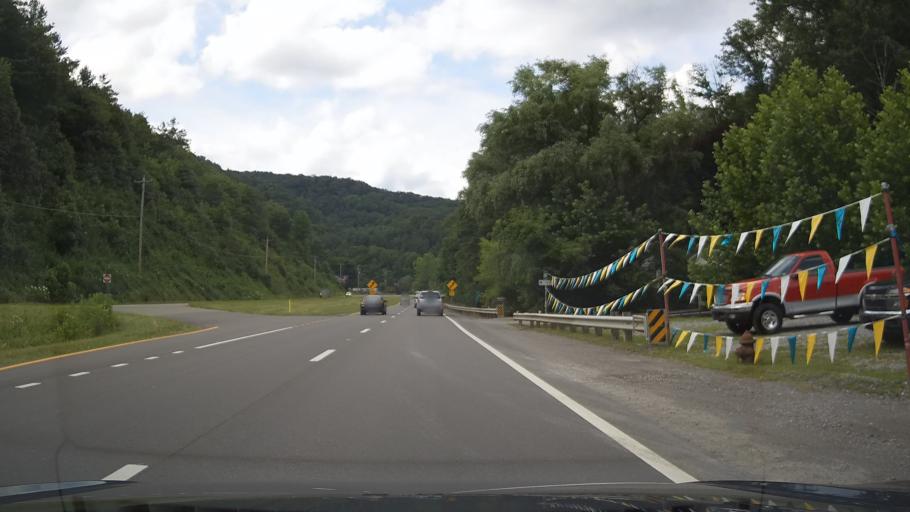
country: US
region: Virginia
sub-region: Wise County
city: Pound
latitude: 37.0573
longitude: -82.6009
